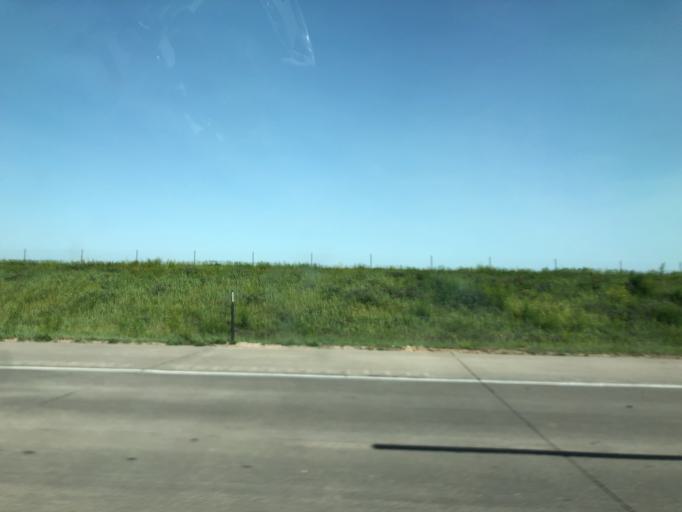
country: US
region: Nebraska
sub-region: Saunders County
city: Ashland
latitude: 40.9769
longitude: -96.3805
